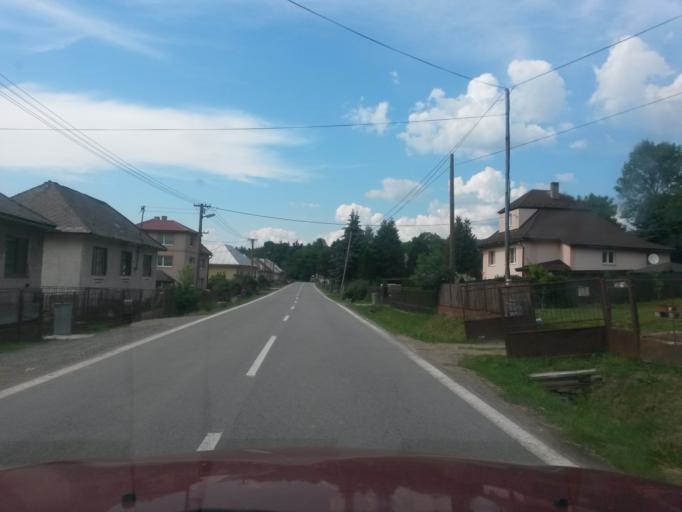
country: SK
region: Presovsky
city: Snina
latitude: 48.9945
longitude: 22.2366
